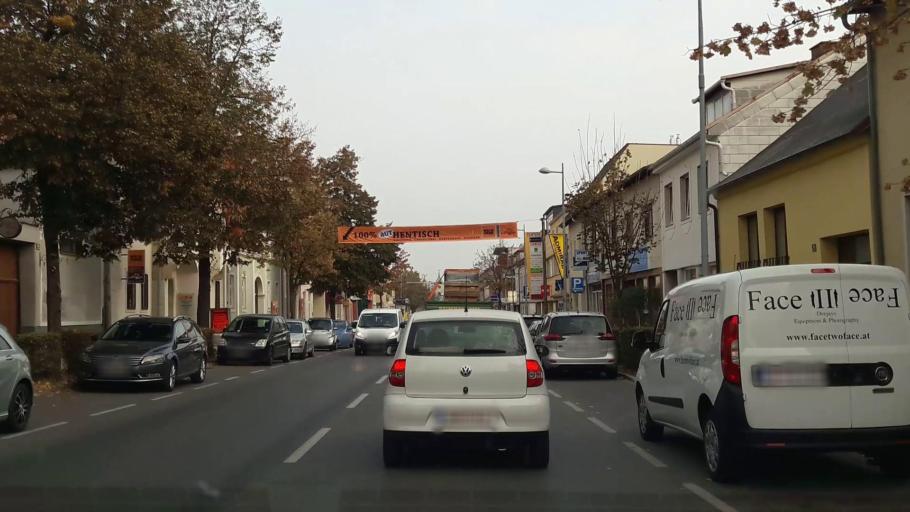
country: AT
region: Burgenland
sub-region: Politischer Bezirk Neusiedl am See
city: Neusiedl am See
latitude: 47.9509
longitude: 16.8383
